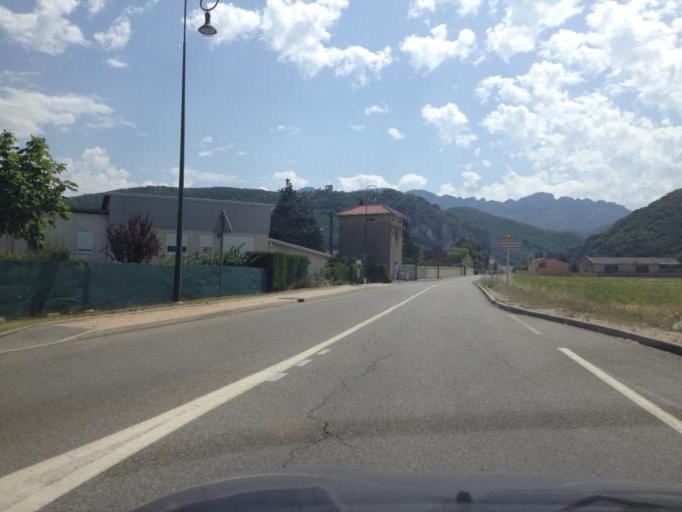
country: FR
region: Rhone-Alpes
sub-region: Departement de la Drome
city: Chatuzange-le-Goubet
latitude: 44.9592
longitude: 5.1325
